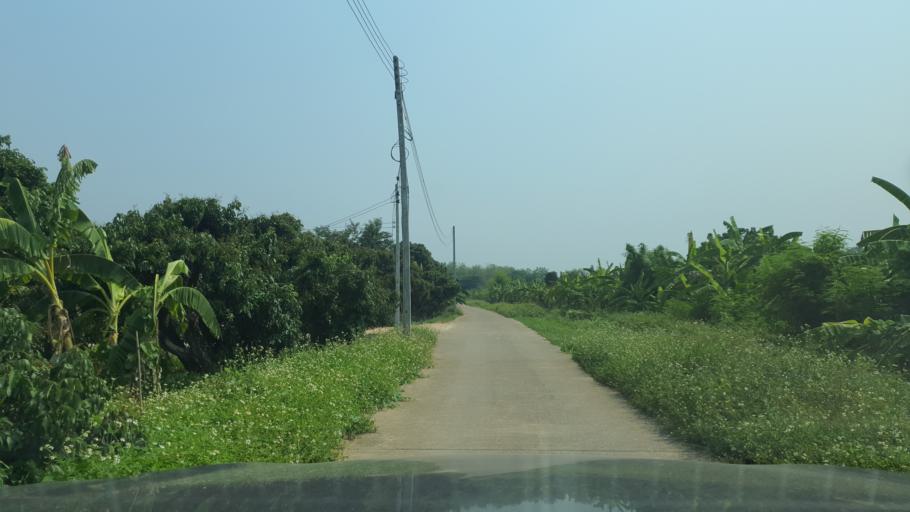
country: TH
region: Chiang Mai
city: Saraphi
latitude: 18.6670
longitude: 98.9904
